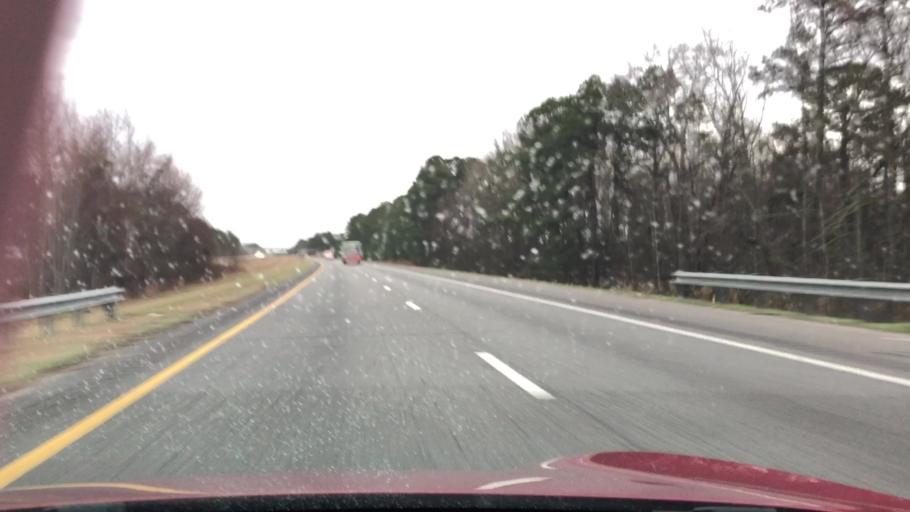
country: US
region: South Carolina
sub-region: Dillon County
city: Latta
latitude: 34.3808
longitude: -79.4745
